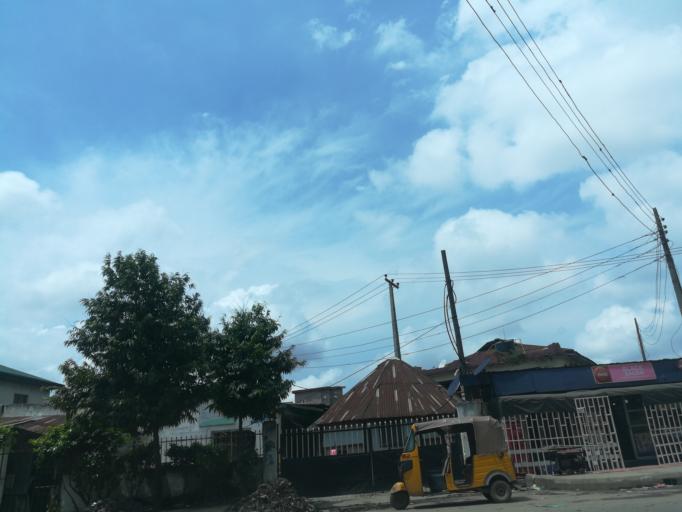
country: NG
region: Lagos
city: Surulere
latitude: 6.5163
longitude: 3.3662
